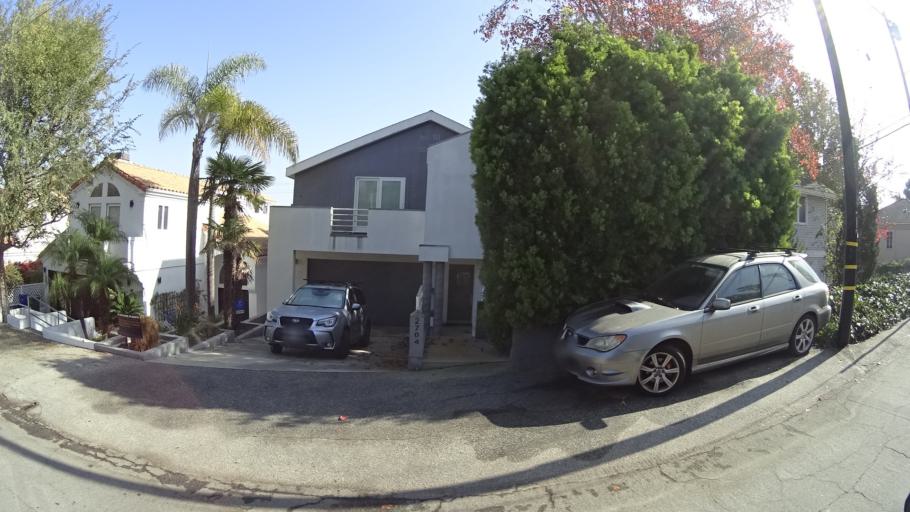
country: US
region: California
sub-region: Los Angeles County
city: Manhattan Beach
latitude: 33.8965
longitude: -118.4044
